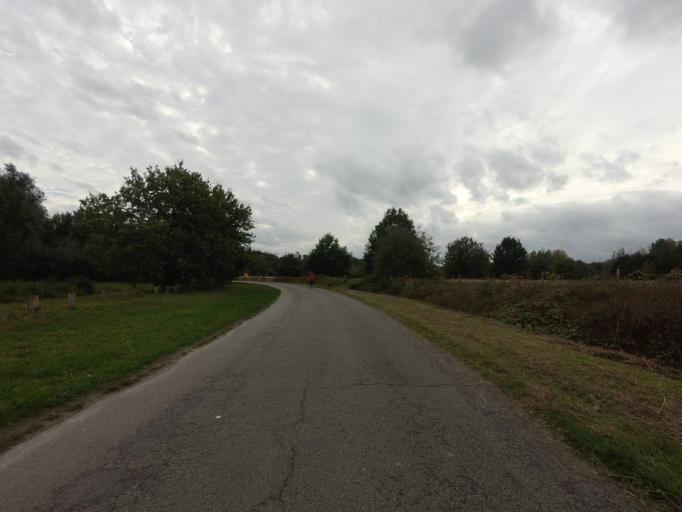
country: NL
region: North Brabant
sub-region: Gemeente Breda
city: Breda
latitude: 51.5597
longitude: 4.8005
